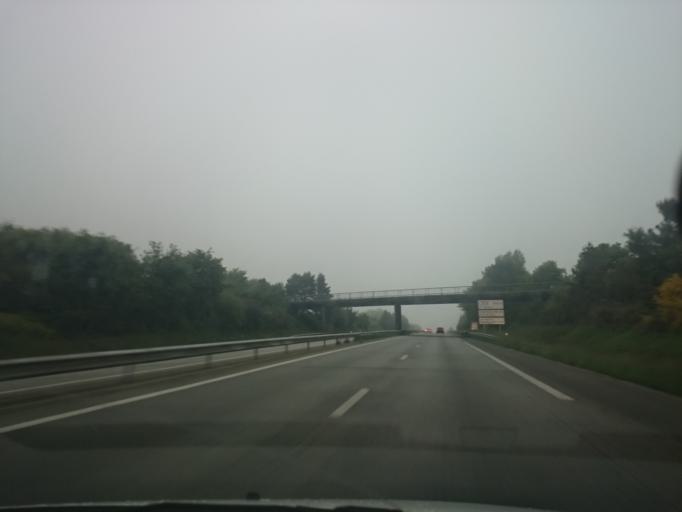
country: FR
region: Brittany
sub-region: Departement du Finistere
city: Briec
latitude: 48.1504
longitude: -4.0355
